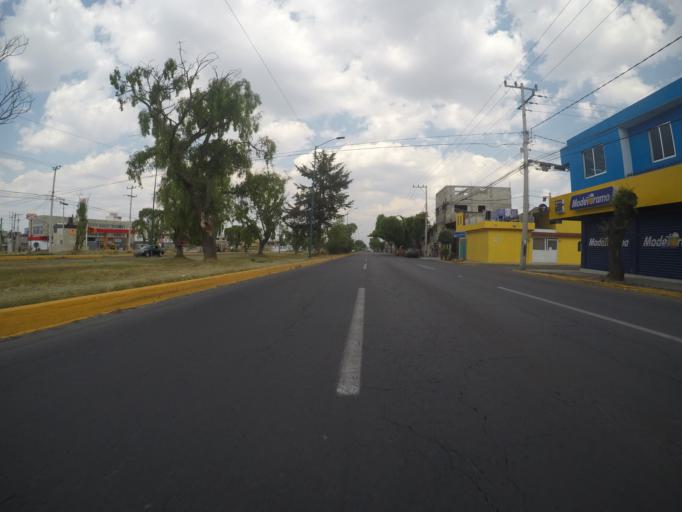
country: MX
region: Mexico
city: San Buenaventura
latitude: 19.2564
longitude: -99.6678
